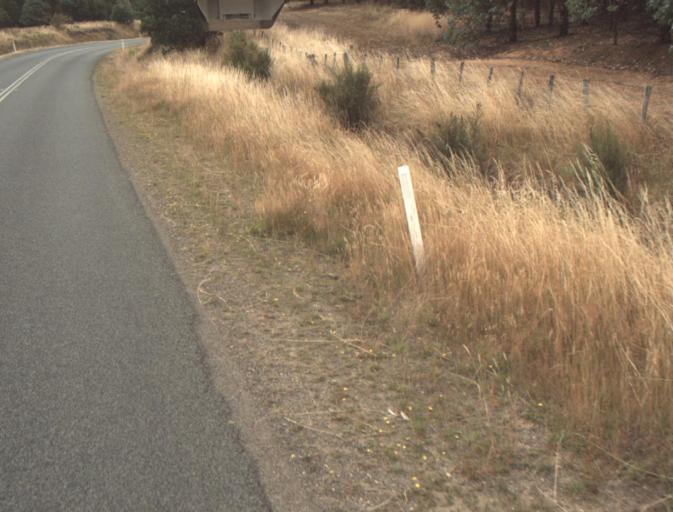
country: AU
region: Tasmania
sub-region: Northern Midlands
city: Evandale
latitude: -41.4753
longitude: 147.5226
